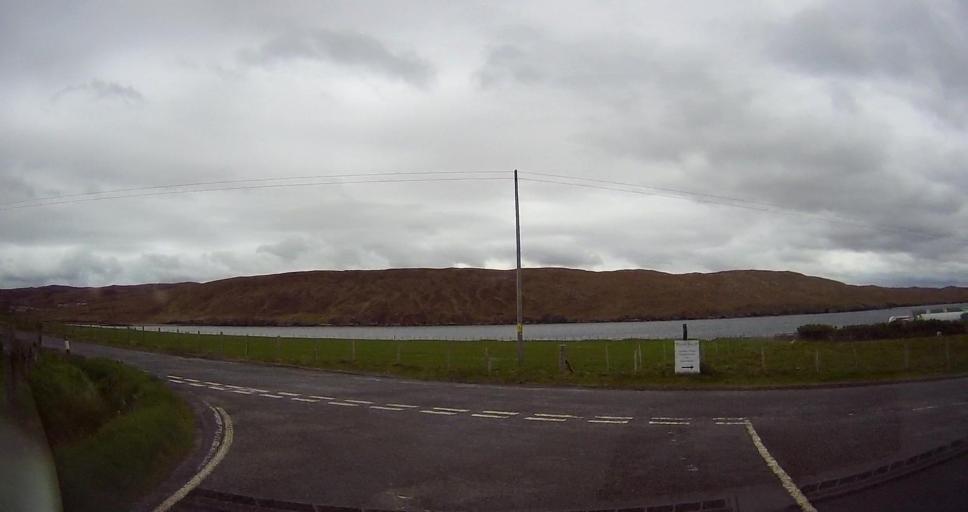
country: GB
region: Scotland
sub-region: Shetland Islands
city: Lerwick
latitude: 60.4833
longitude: -1.4740
